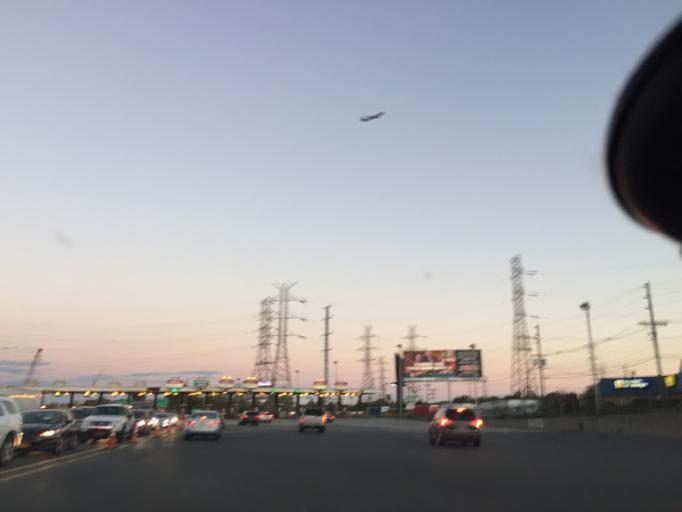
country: US
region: New Jersey
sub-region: Union County
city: Elizabeth
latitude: 40.6413
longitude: -74.2114
